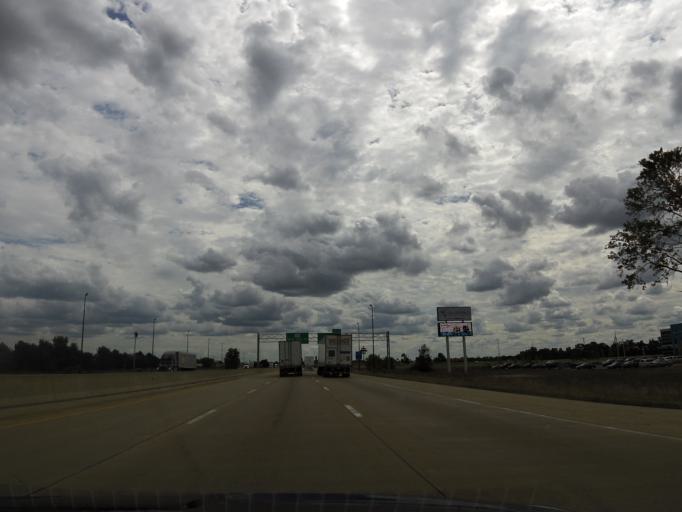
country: US
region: Illinois
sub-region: Winnebago County
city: South Beloit
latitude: 42.4630
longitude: -88.9952
